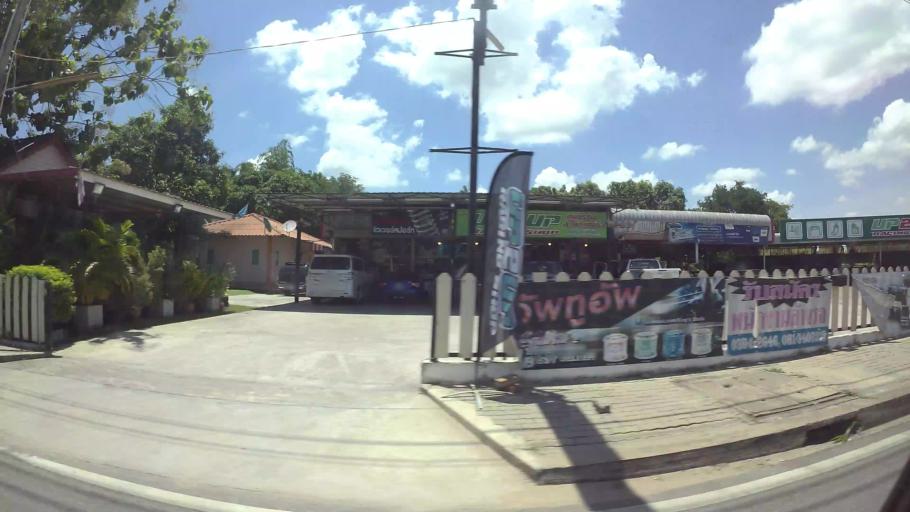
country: TH
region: Chon Buri
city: Si Racha
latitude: 13.1253
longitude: 100.9436
